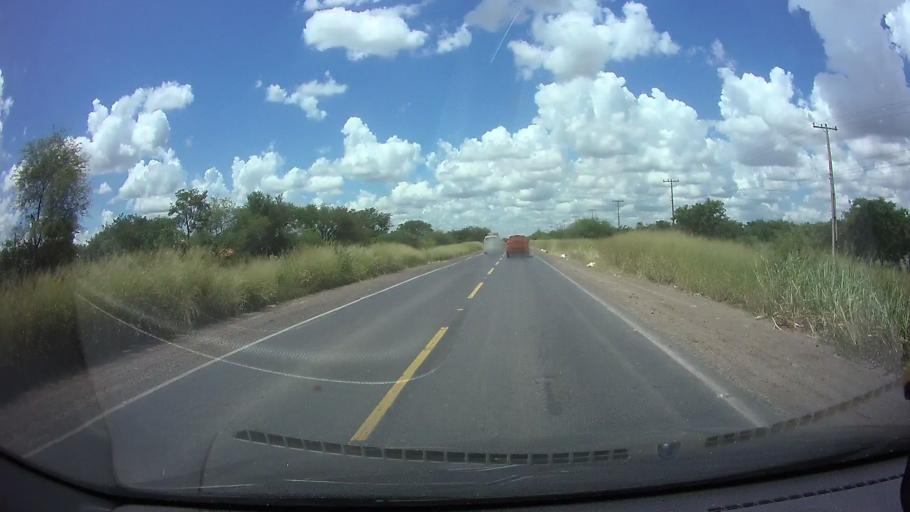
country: PY
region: Central
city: Colonia Mariano Roque Alonso
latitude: -25.1892
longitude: -57.6106
